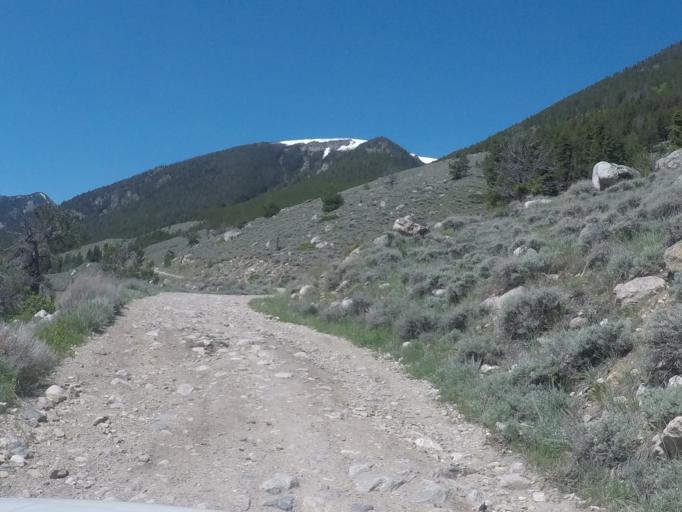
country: US
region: Montana
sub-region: Carbon County
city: Red Lodge
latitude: 45.0598
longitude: -109.4171
